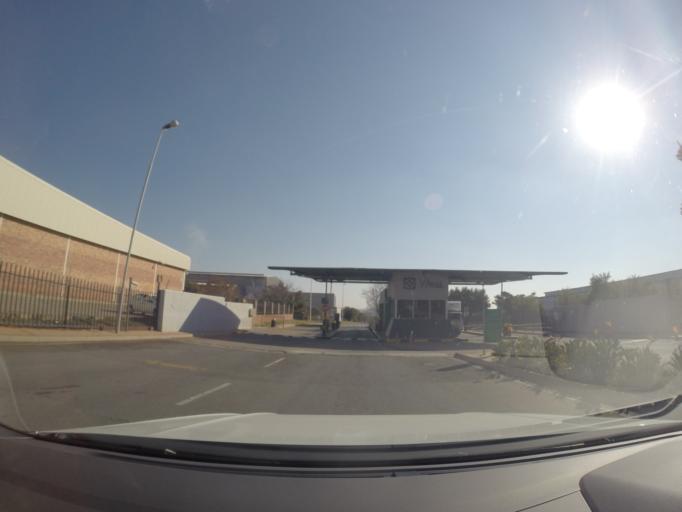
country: ZA
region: Gauteng
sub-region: City of Johannesburg Metropolitan Municipality
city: Modderfontein
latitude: -26.0906
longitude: 28.1222
